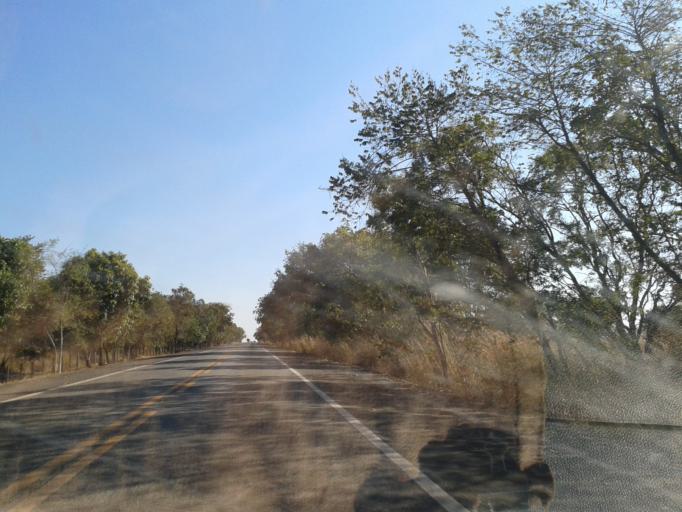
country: BR
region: Goias
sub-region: Mozarlandia
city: Mozarlandia
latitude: -14.8135
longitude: -50.5320
